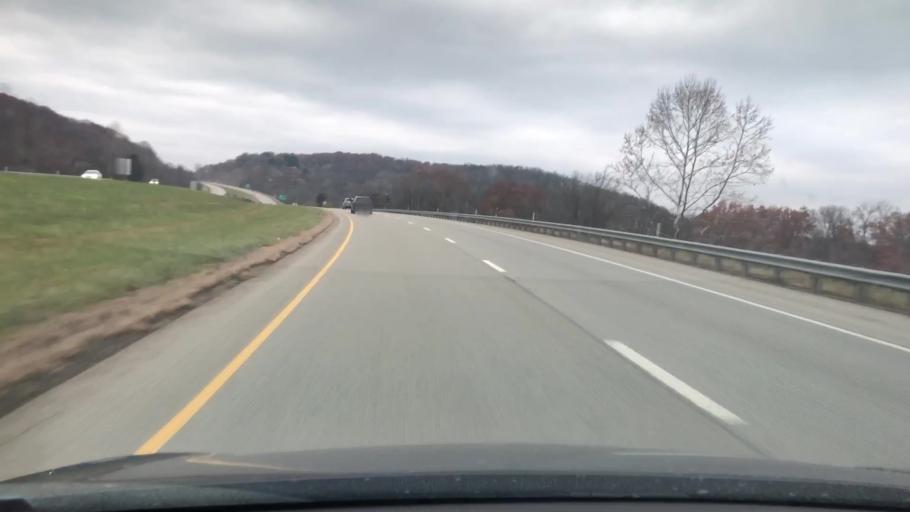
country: US
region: Pennsylvania
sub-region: Armstrong County
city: West Kittanning
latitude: 40.8023
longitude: -79.5329
